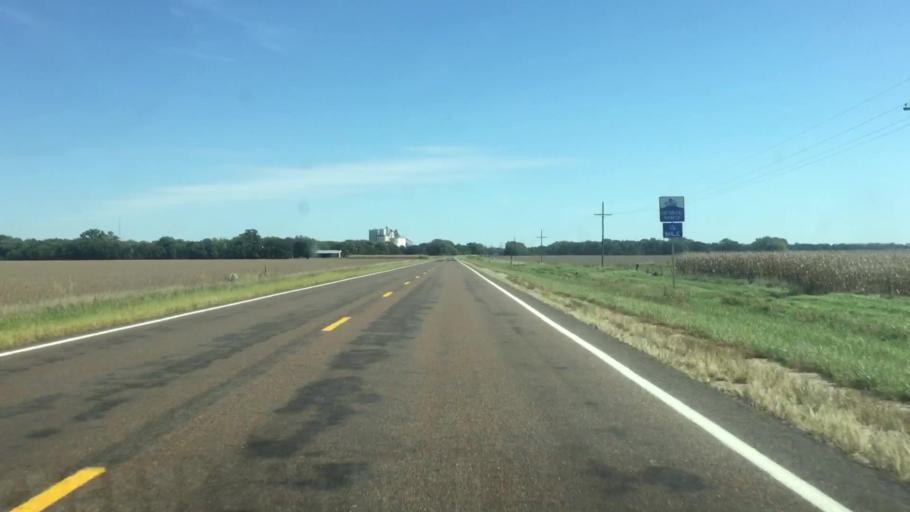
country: US
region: Nebraska
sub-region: Gage County
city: Wymore
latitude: 40.0456
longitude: -96.8183
